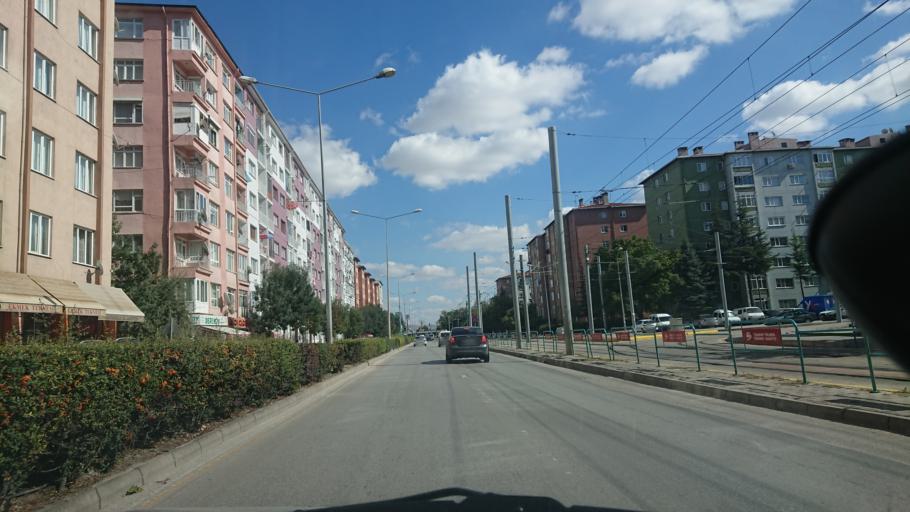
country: TR
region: Eskisehir
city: Eskisehir
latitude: 39.7650
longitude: 30.5529
